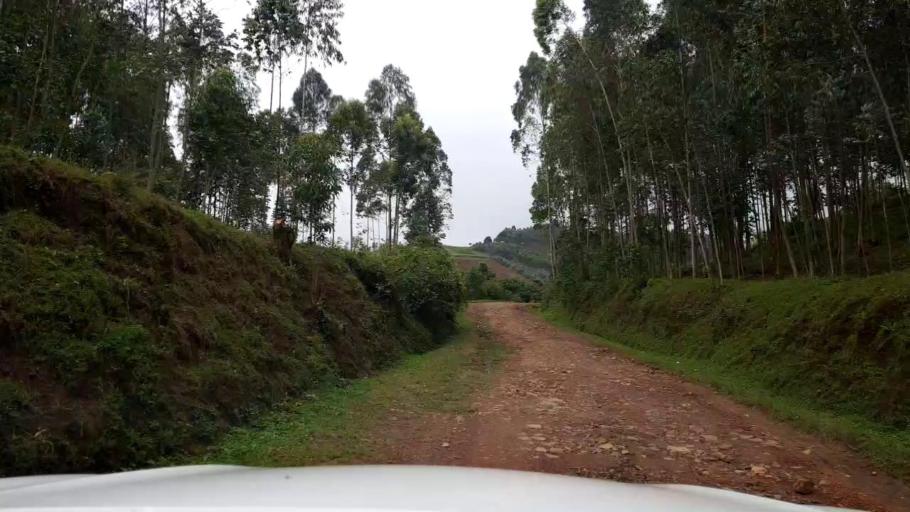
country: RW
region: Northern Province
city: Musanze
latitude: -1.6060
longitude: 29.7672
